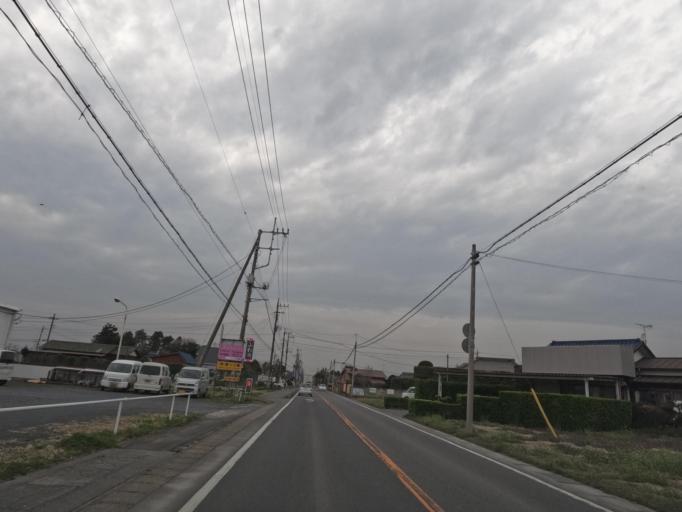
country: JP
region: Ibaraki
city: Toride
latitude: 35.9467
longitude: 140.0578
